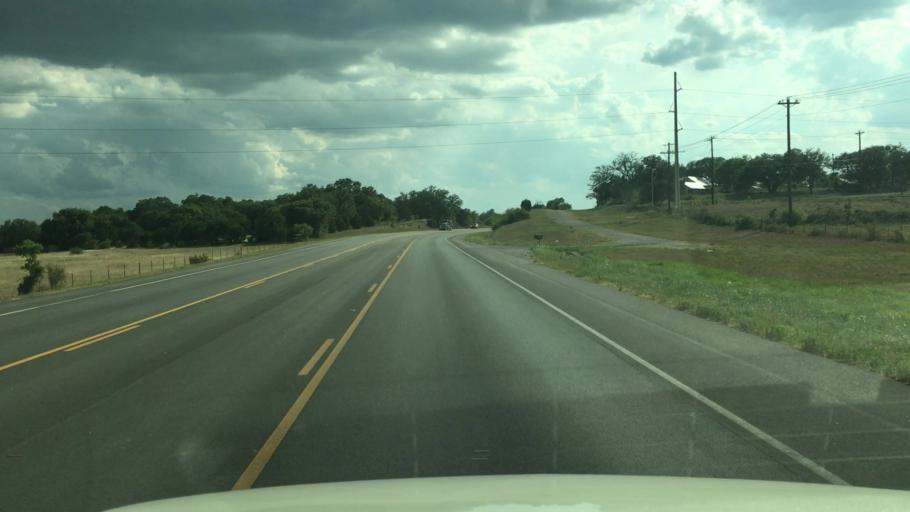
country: US
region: Texas
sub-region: Hays County
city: Dripping Springs
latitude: 30.2027
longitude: -98.1528
